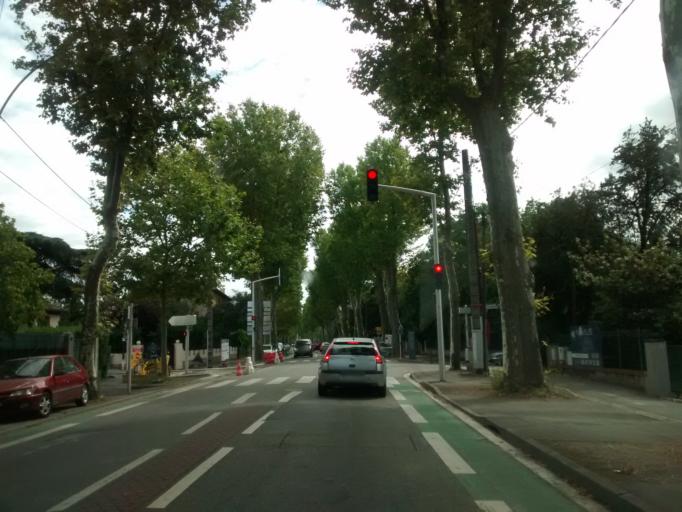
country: FR
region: Midi-Pyrenees
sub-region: Departement de la Haute-Garonne
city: L'Union
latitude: 43.6409
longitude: 1.4664
